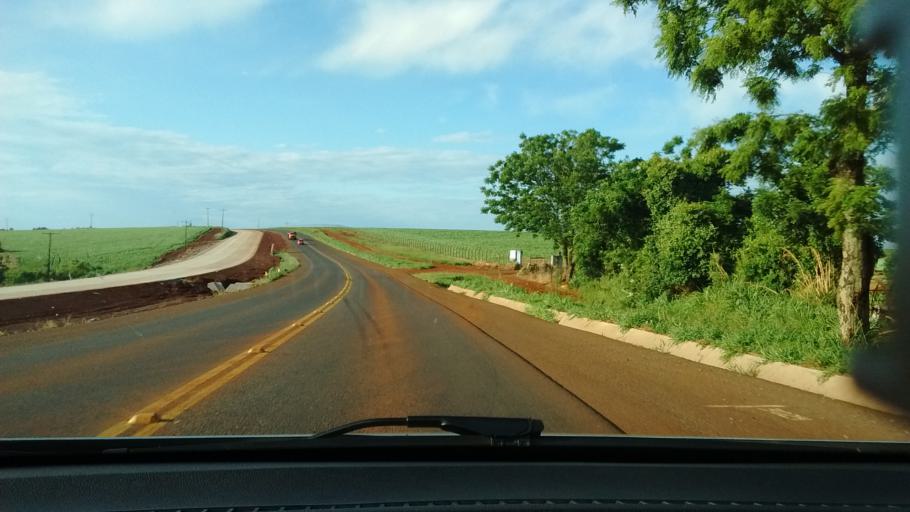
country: BR
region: Parana
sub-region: Cascavel
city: Cascavel
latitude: -25.1232
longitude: -53.5871
